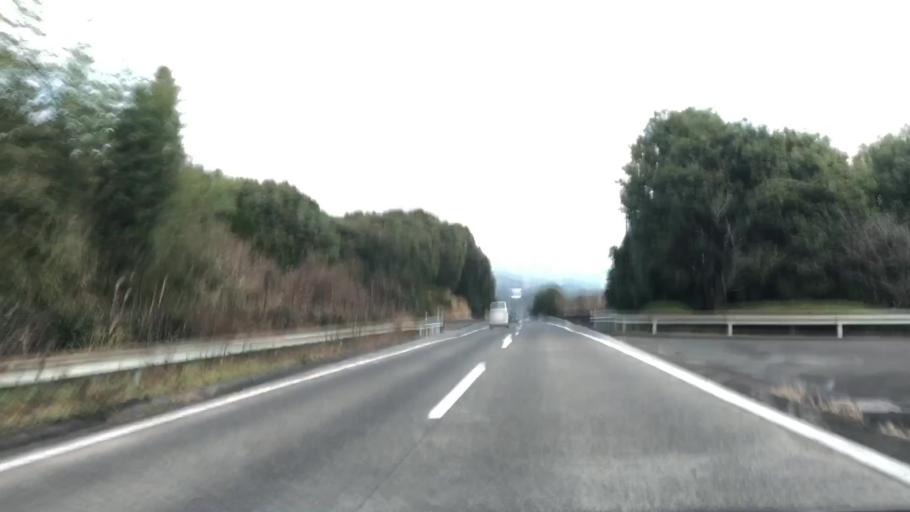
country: JP
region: Saga Prefecture
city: Kanzakimachi-kanzaki
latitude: 33.3414
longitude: 130.3564
